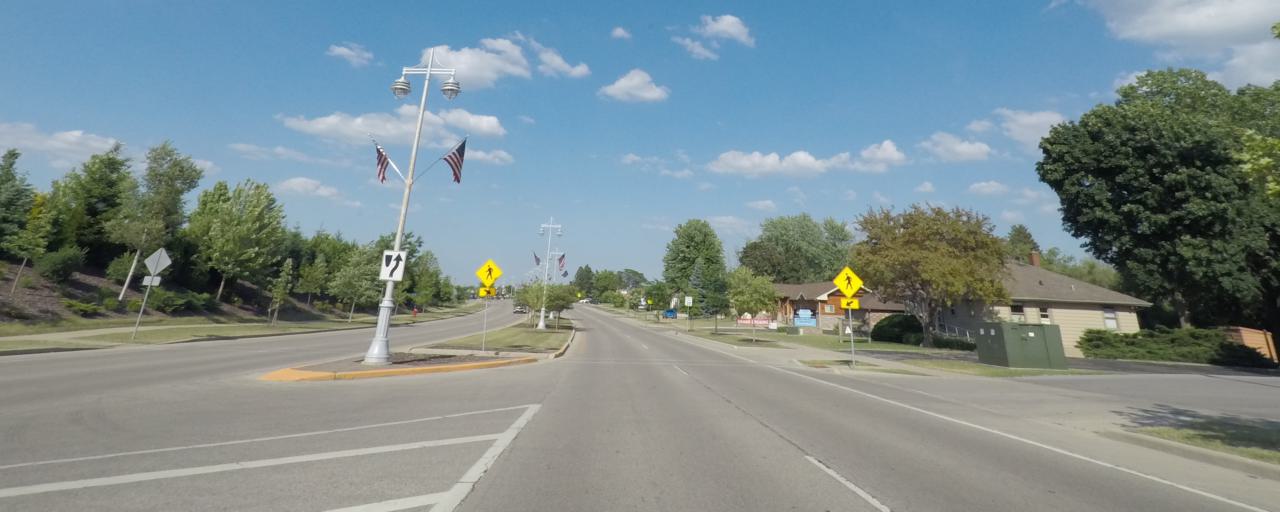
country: US
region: Wisconsin
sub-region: Waukesha County
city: Muskego
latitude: 42.9066
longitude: -88.1352
